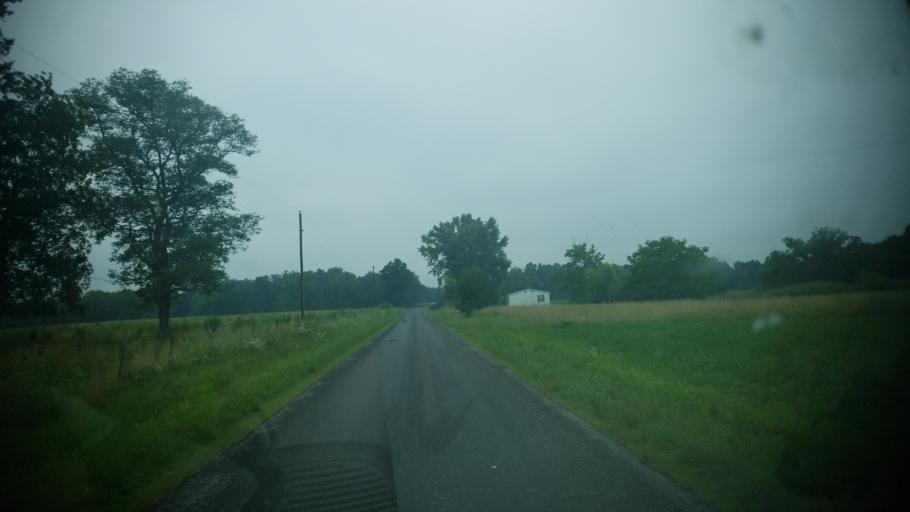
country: US
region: Illinois
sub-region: Clay County
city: Flora
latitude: 38.5791
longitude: -88.3647
